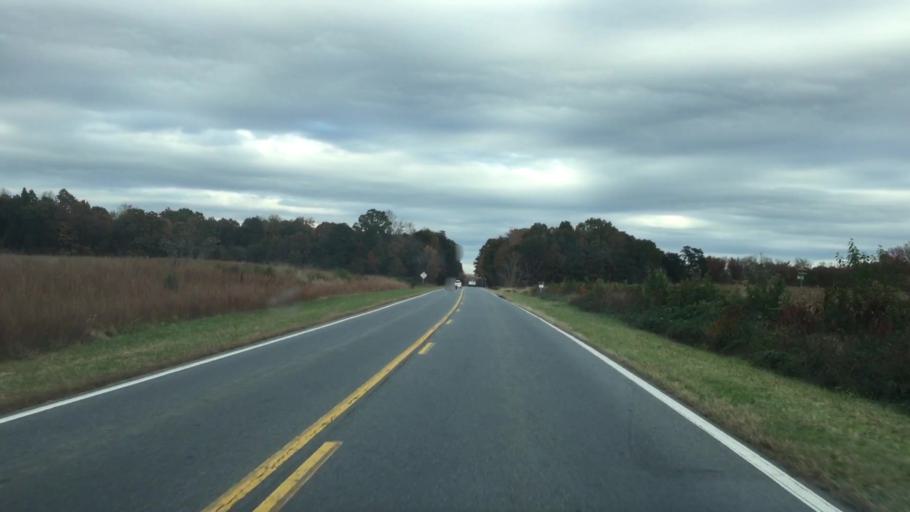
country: US
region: North Carolina
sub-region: Rockingham County
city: Reidsville
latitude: 36.2919
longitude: -79.7296
